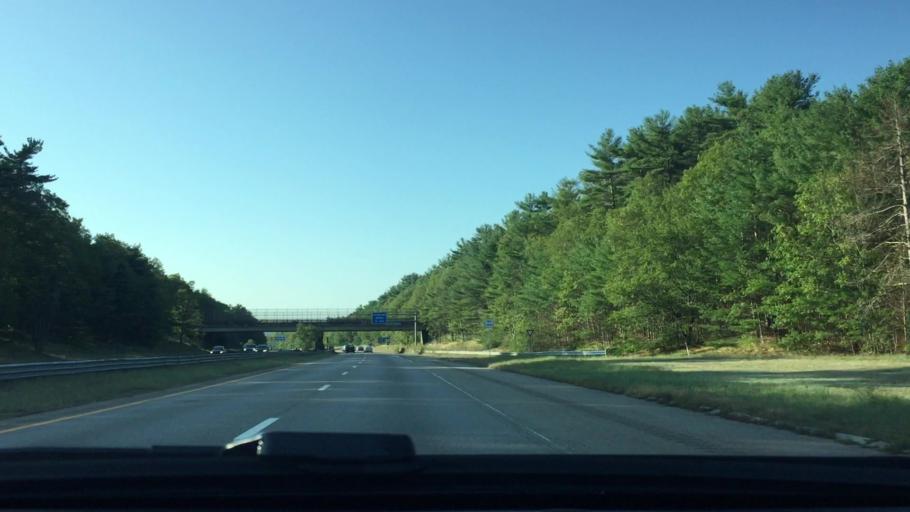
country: US
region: Massachusetts
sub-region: Plymouth County
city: Kingston
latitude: 42.0156
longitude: -70.7266
